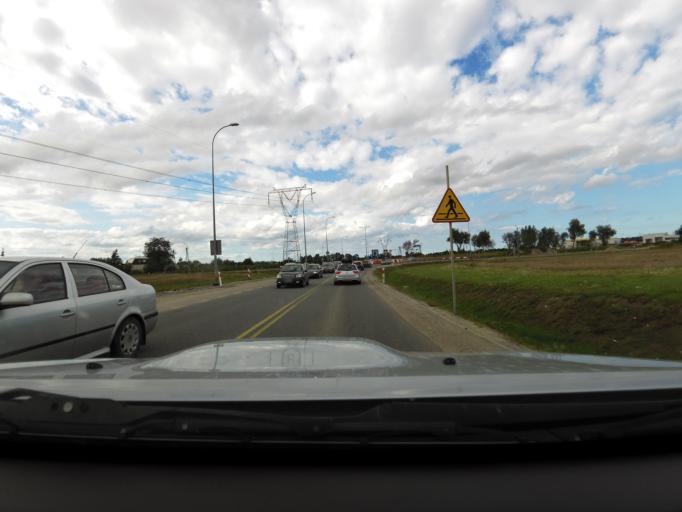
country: PL
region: Pomeranian Voivodeship
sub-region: Powiat gdanski
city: Cedry Wielkie
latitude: 54.2729
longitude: 18.8692
